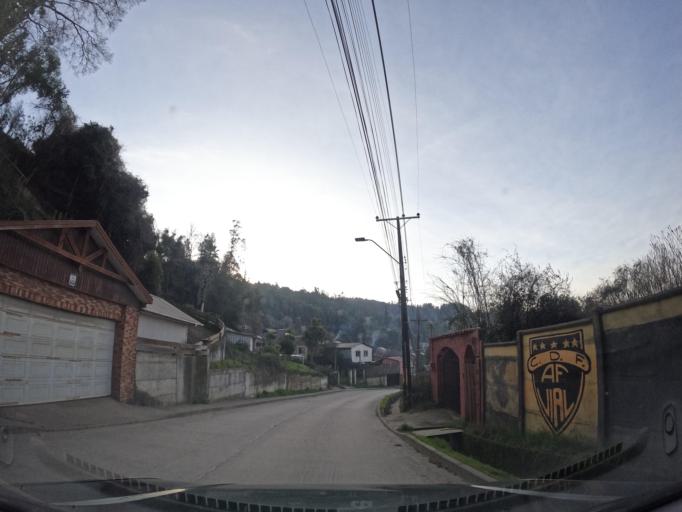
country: CL
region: Biobio
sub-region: Provincia de Concepcion
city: Concepcion
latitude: -36.8443
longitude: -73.0103
